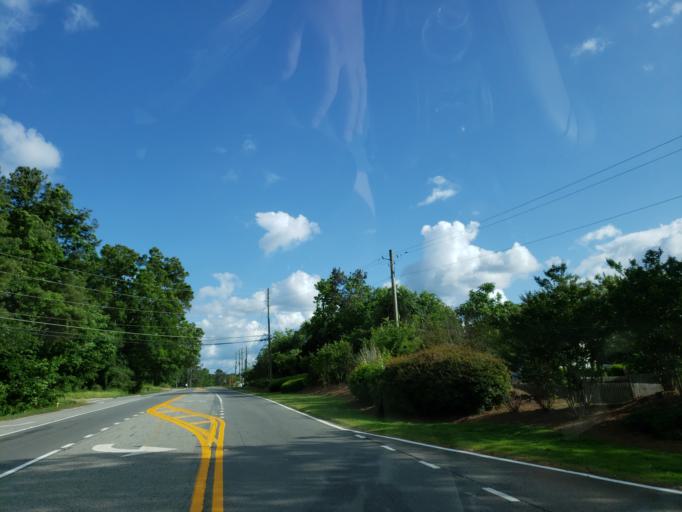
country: US
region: Georgia
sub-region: Bartow County
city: Cartersville
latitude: 34.2269
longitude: -84.8568
